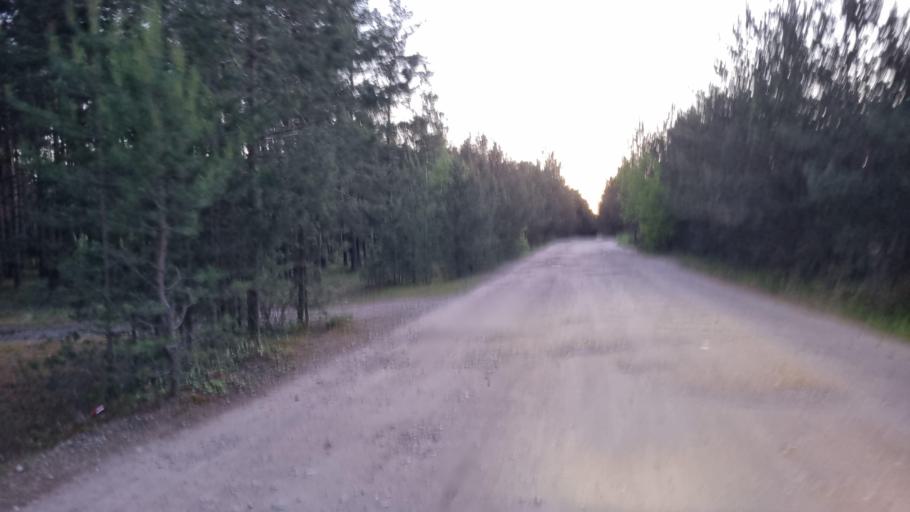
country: LV
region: Riga
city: Daugavgriva
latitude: 57.0213
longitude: 24.0327
